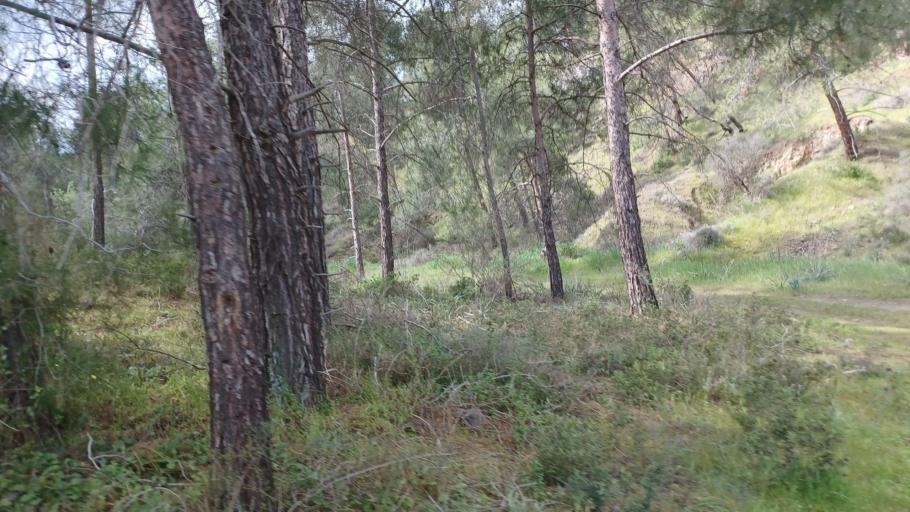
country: CY
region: Lefkosia
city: Astromeritis
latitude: 35.0736
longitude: 32.9614
